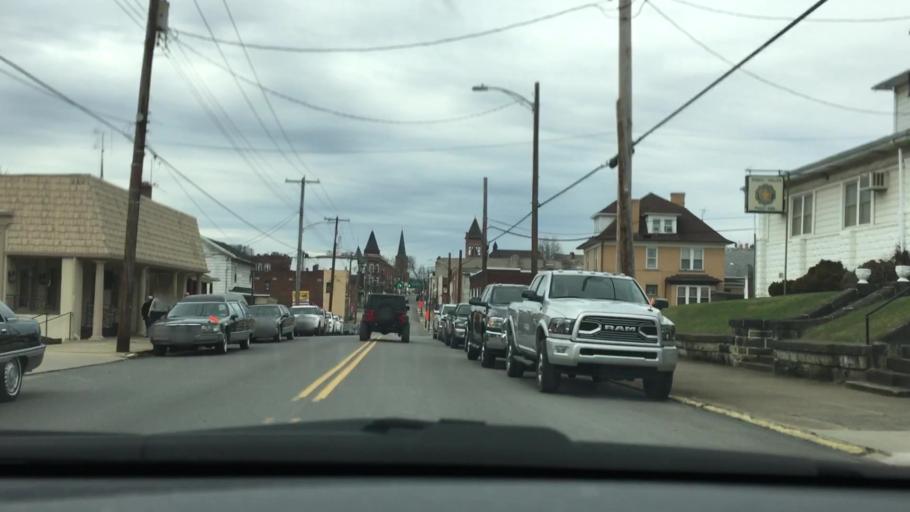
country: US
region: Pennsylvania
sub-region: Washington County
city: McDonald
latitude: 40.3700
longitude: -80.2326
